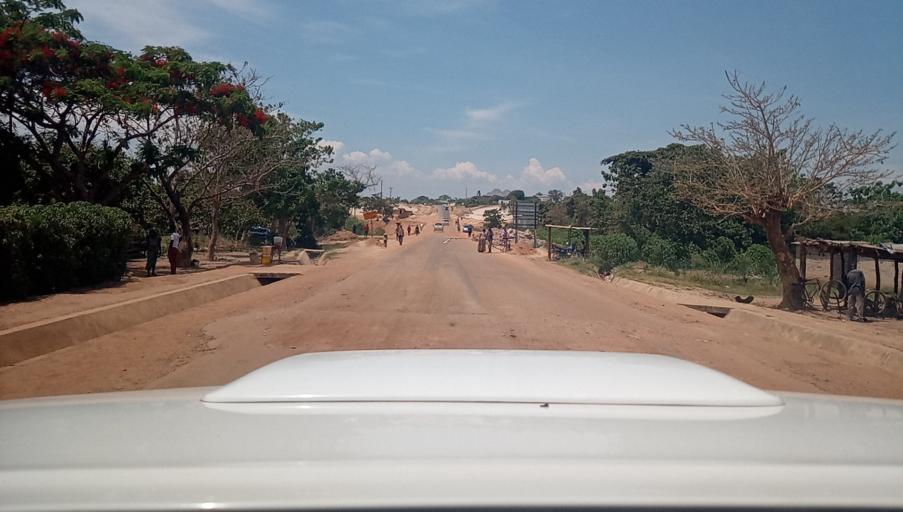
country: ZM
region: Luapula
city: Samfya
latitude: -11.3547
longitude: 29.5582
